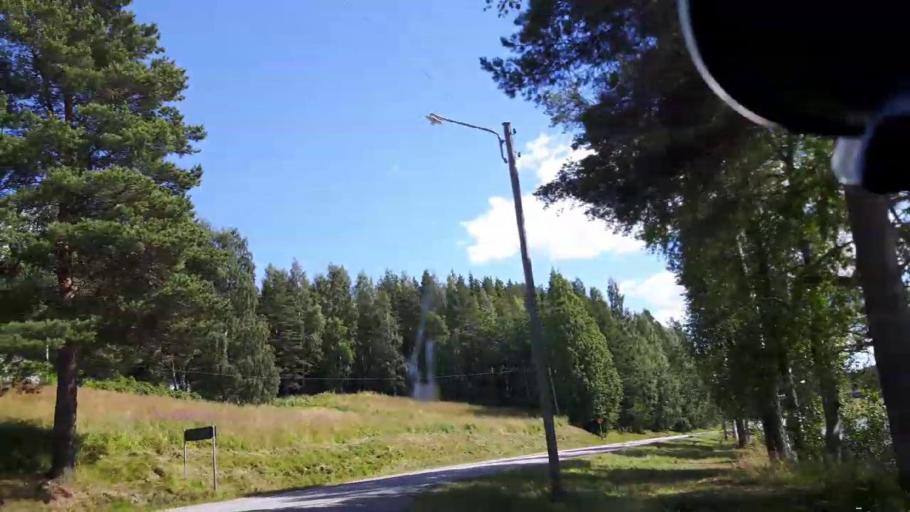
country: SE
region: Jaemtland
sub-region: Ragunda Kommun
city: Hammarstrand
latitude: 62.9679
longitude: 16.0956
